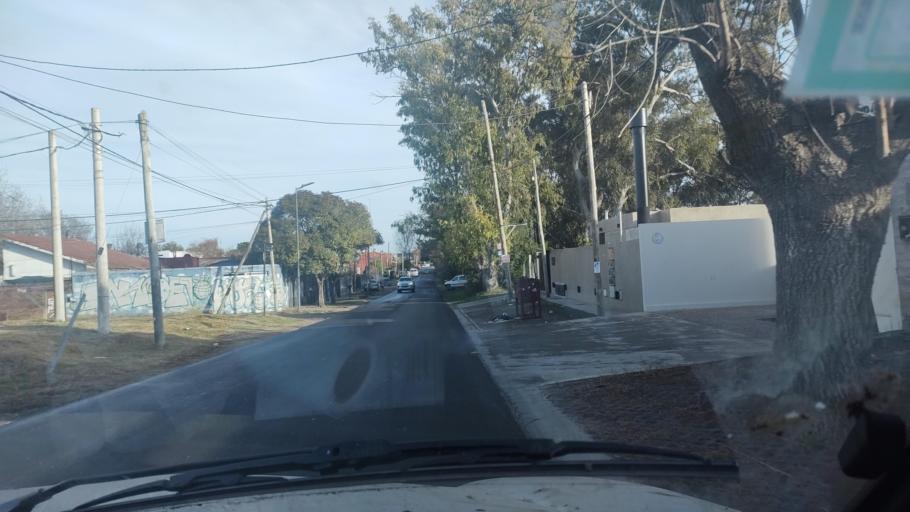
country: AR
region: Buenos Aires
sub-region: Partido de La Plata
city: La Plata
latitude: -34.8992
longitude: -58.0391
